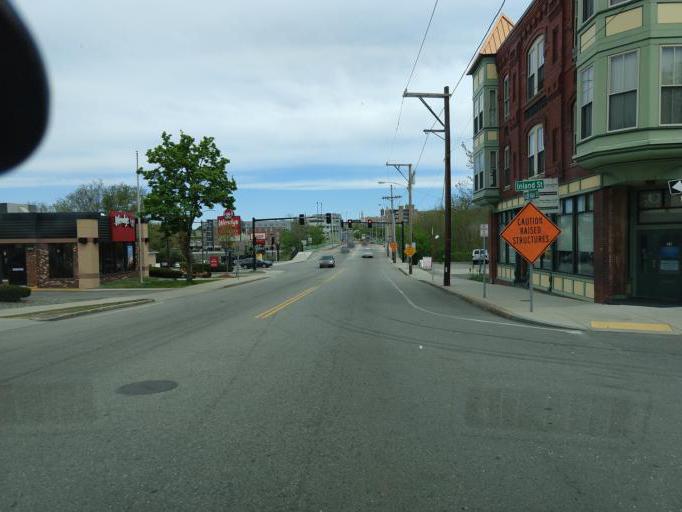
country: US
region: Massachusetts
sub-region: Essex County
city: Haverhill
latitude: 42.7716
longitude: -71.0757
